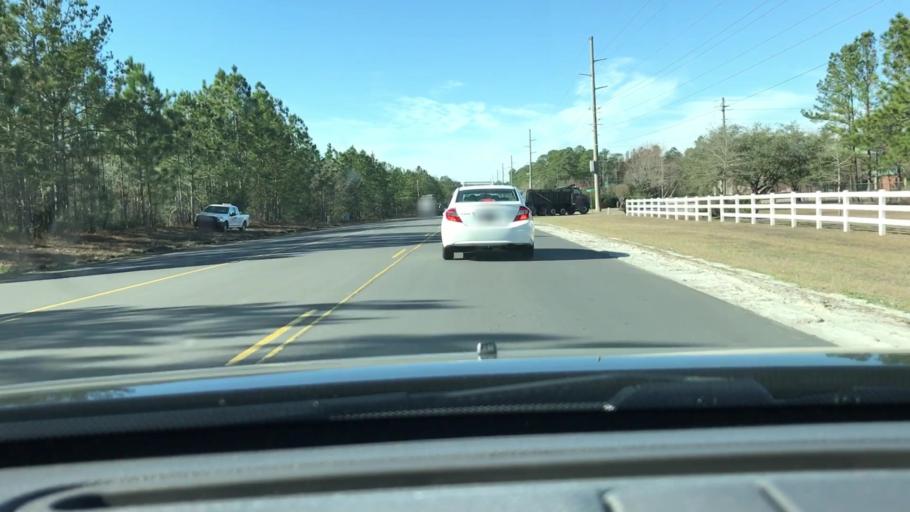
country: US
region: North Carolina
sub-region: Brunswick County
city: Shallotte
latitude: 33.9801
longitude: -78.4128
